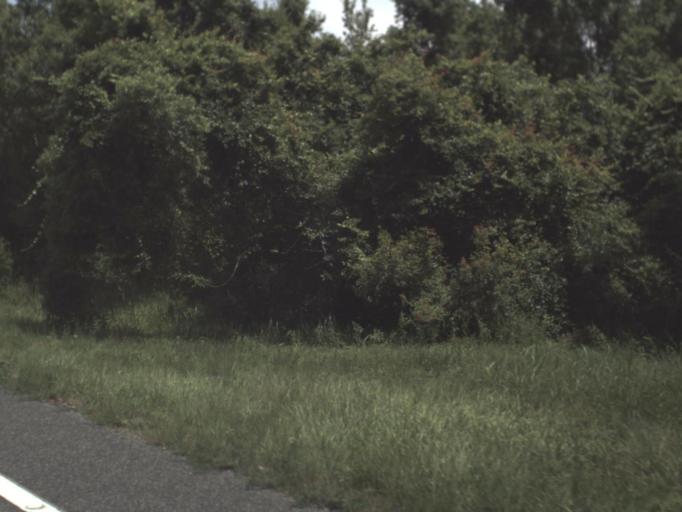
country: US
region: Florida
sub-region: Taylor County
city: Steinhatchee
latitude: 29.8215
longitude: -83.3529
